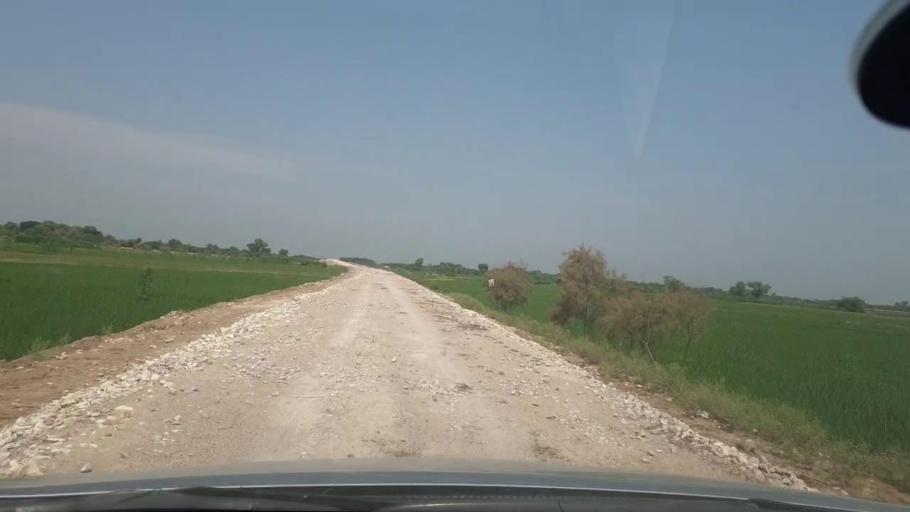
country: PK
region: Balochistan
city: Garhi Khairo
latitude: 28.0588
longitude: 67.9995
